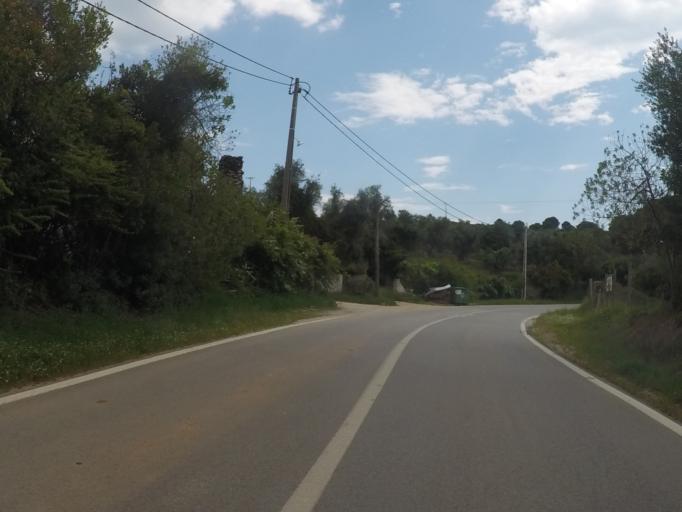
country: PT
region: Setubal
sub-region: Sesimbra
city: Sesimbra
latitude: 38.4733
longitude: -9.0295
